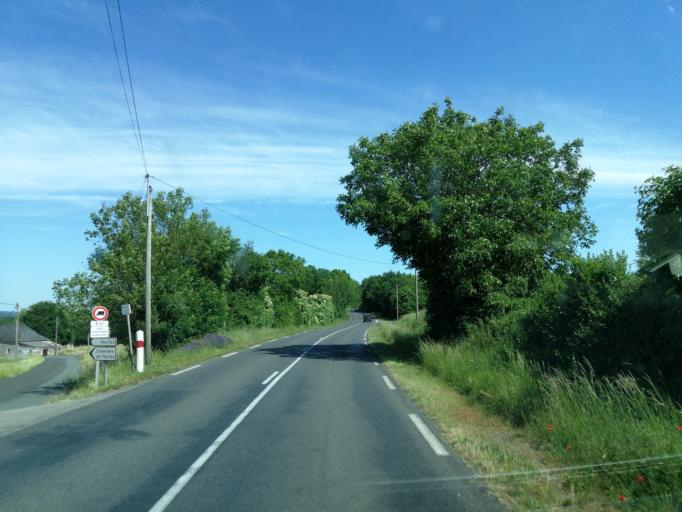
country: FR
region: Poitou-Charentes
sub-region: Departement des Deux-Sevres
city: Saint-Jean-de-Thouars
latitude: 46.9740
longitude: -0.1758
